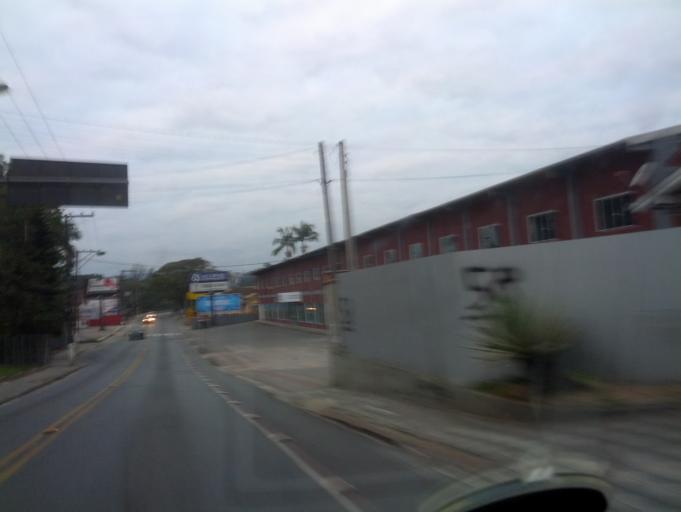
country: BR
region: Santa Catarina
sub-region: Blumenau
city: Blumenau
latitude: -26.8894
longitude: -49.0868
